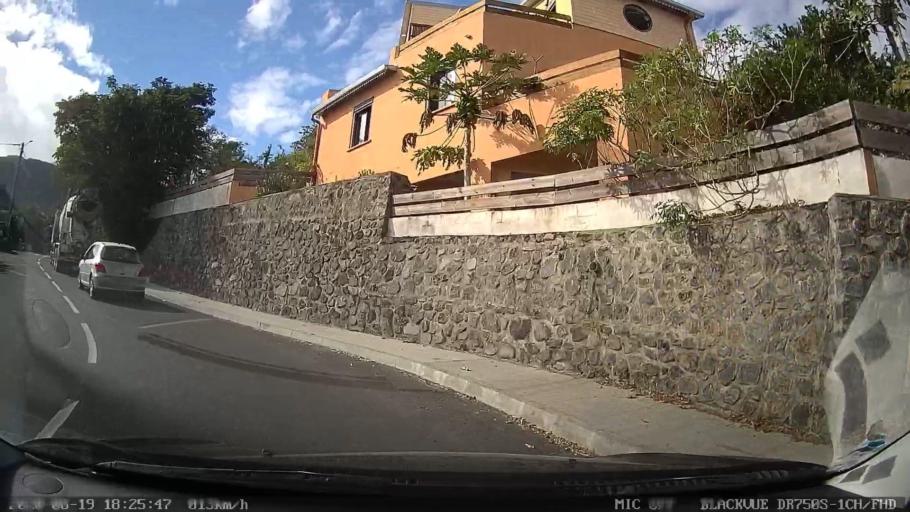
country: RE
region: Reunion
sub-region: Reunion
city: La Possession
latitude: -20.9539
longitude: 55.3498
